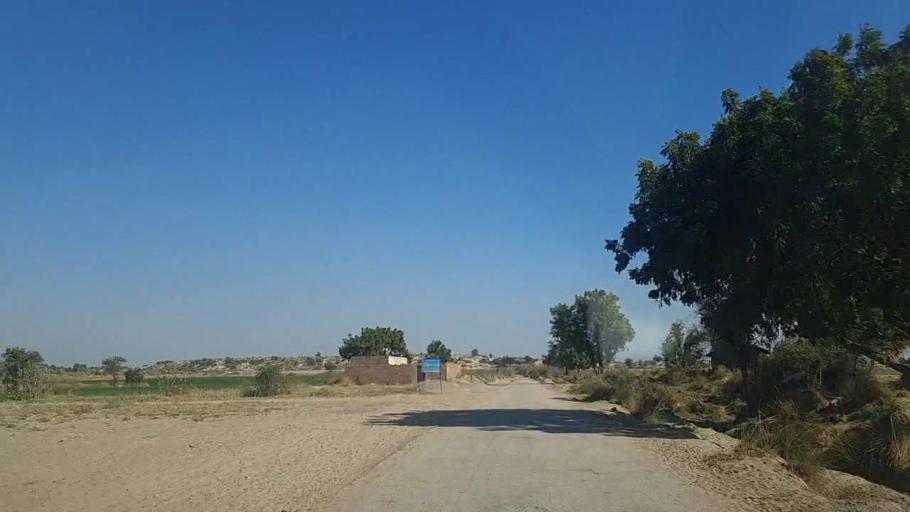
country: PK
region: Sindh
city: Sanghar
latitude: 26.2092
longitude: 68.9251
